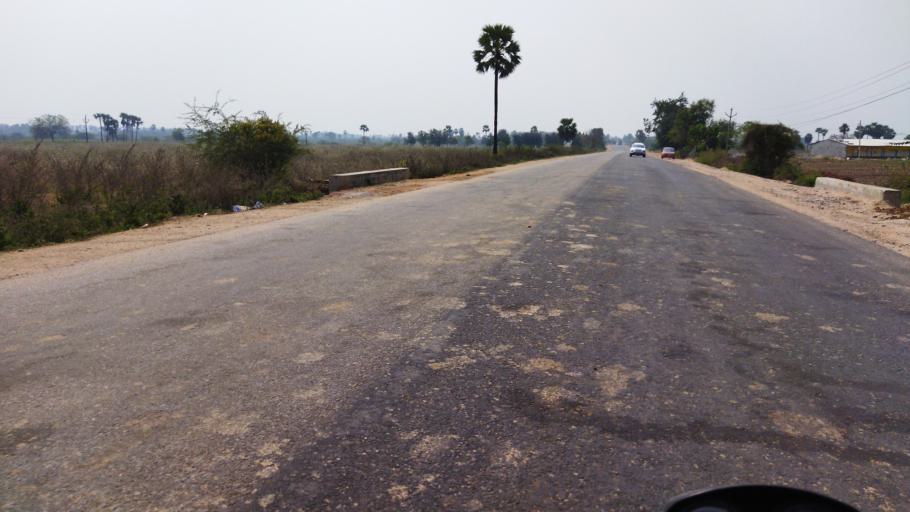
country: IN
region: Telangana
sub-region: Nalgonda
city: Nalgonda
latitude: 17.1052
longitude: 79.3474
